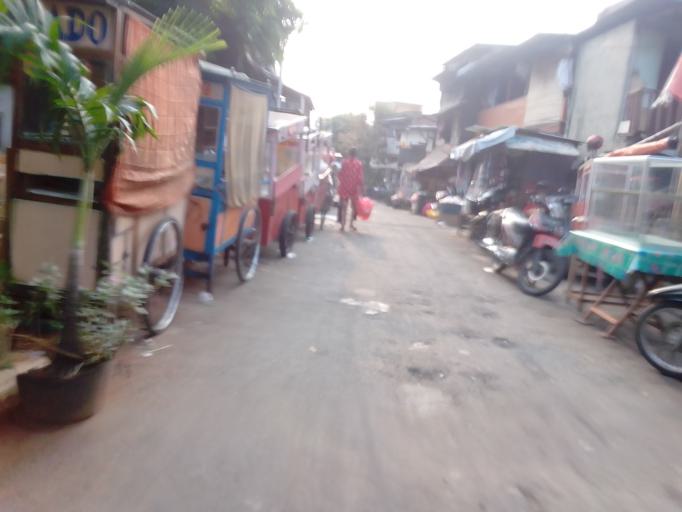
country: ID
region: Jakarta Raya
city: Jakarta
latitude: -6.1926
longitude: 106.8123
